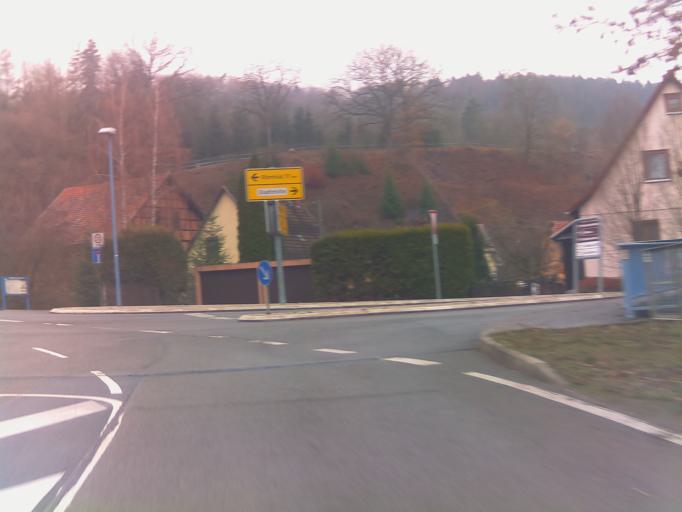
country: DE
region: Thuringia
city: Themar
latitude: 50.5012
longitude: 10.6119
